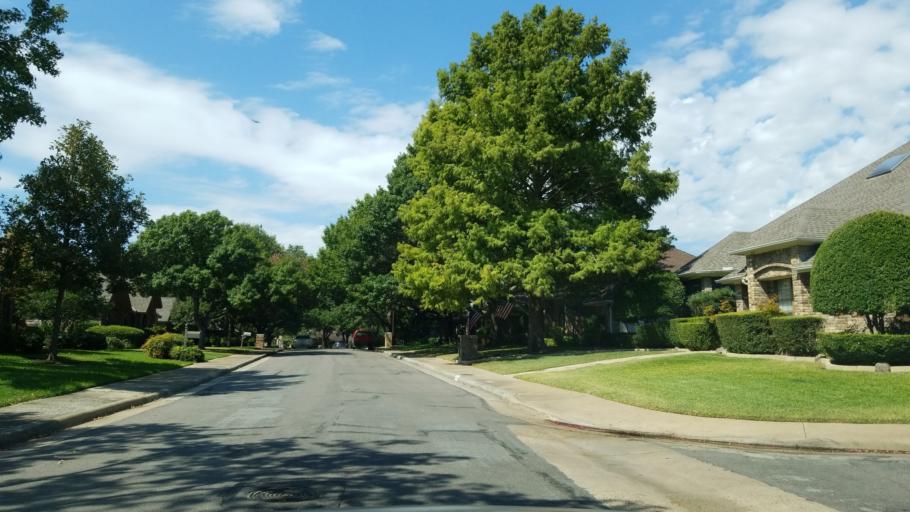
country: US
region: Texas
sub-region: Dallas County
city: Addison
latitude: 32.9556
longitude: -96.7989
